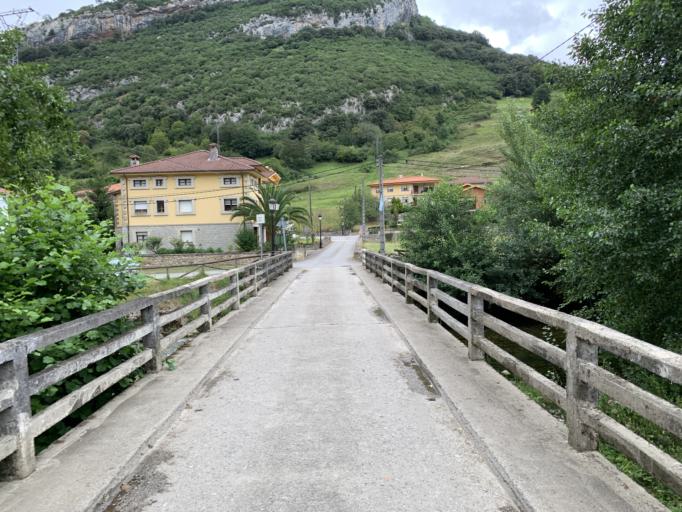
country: ES
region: Asturias
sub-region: Province of Asturias
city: Carrena
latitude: 43.3086
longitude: -4.8358
